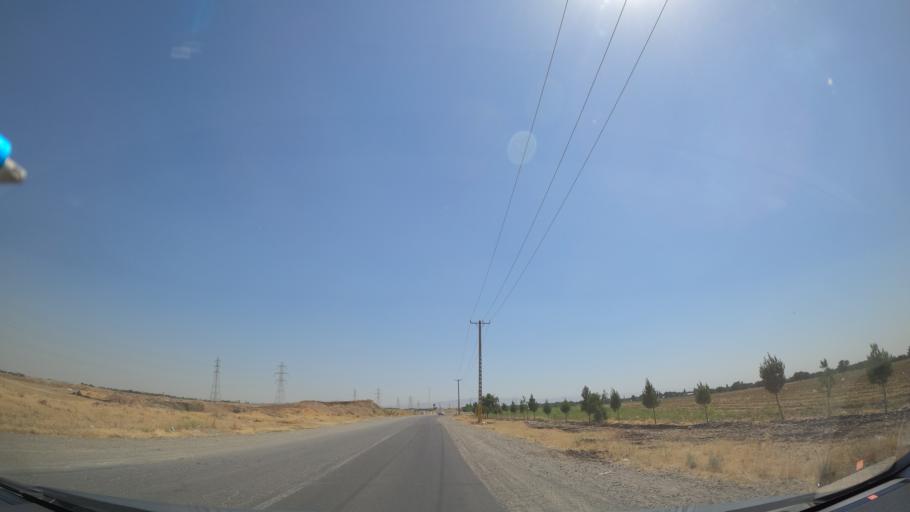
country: IR
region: Alborz
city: Hashtgerd
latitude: 35.9216
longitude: 50.7398
